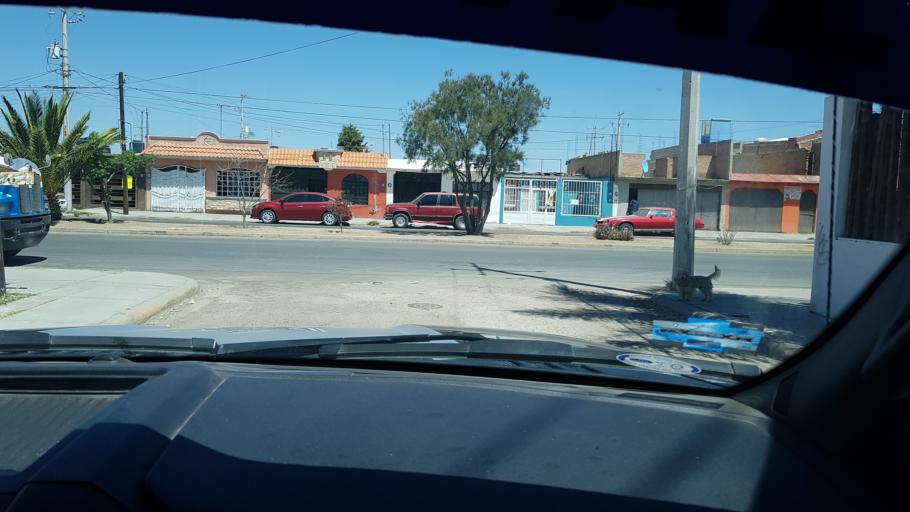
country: MX
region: Durango
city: Victoria de Durango
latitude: 24.0536
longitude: -104.5978
